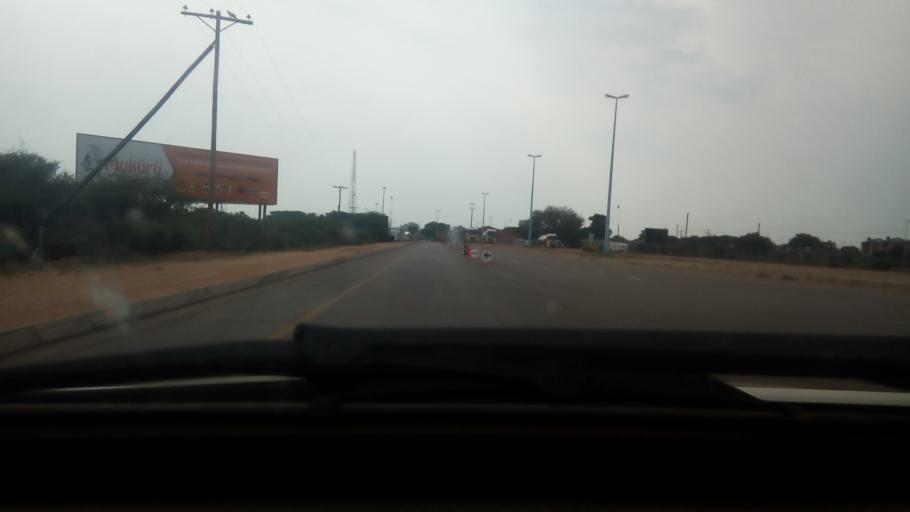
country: BW
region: South East
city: Gaborone
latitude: -24.7025
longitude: 26.0891
